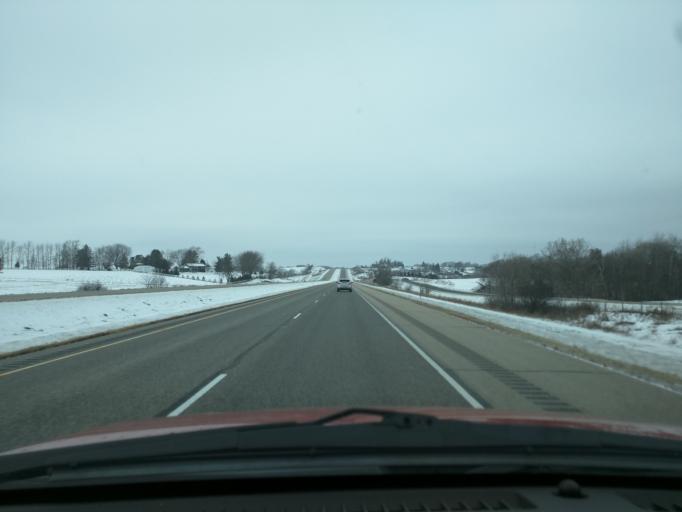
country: US
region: Minnesota
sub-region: Winona County
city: Winona
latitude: 43.9426
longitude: -91.6351
